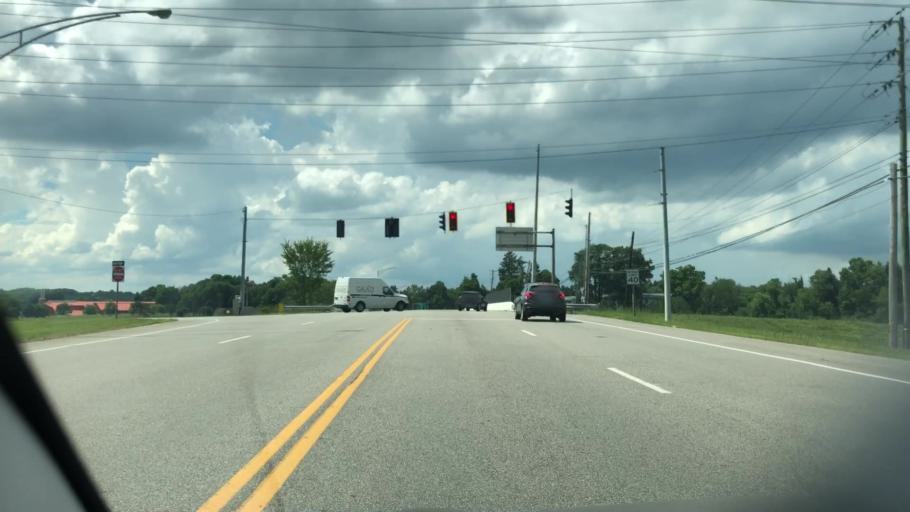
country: US
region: Ohio
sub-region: Summit County
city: Montrose-Ghent
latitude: 41.1497
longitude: -81.6292
